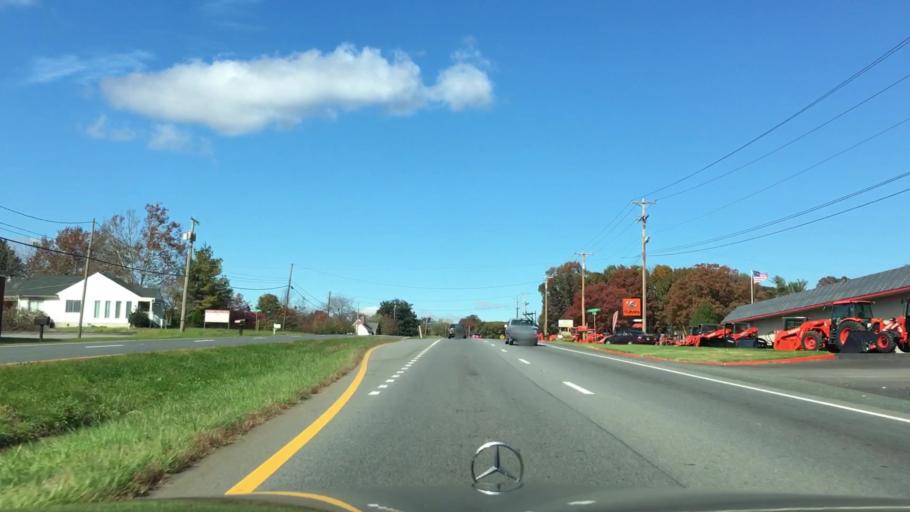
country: US
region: Virginia
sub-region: Campbell County
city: Timberlake
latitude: 37.3141
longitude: -79.1858
